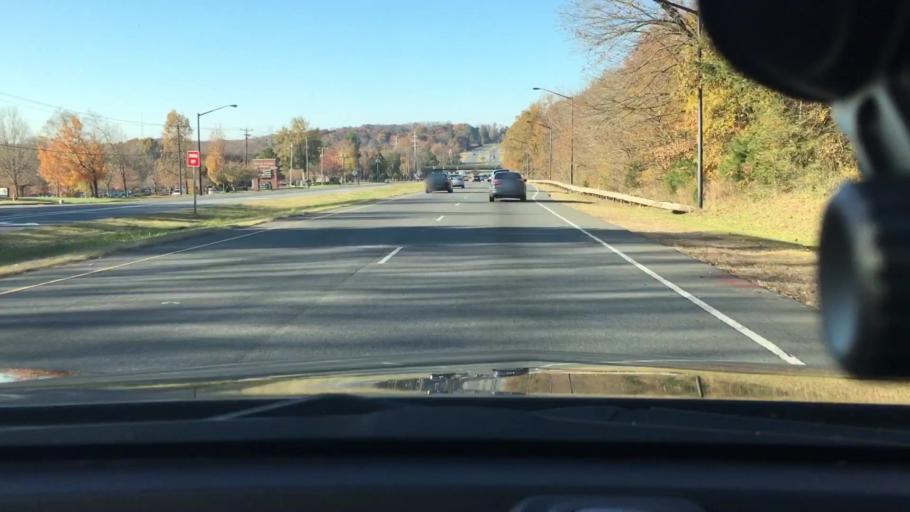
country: US
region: North Carolina
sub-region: Cabarrus County
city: Harrisburg
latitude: 35.2985
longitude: -80.7376
